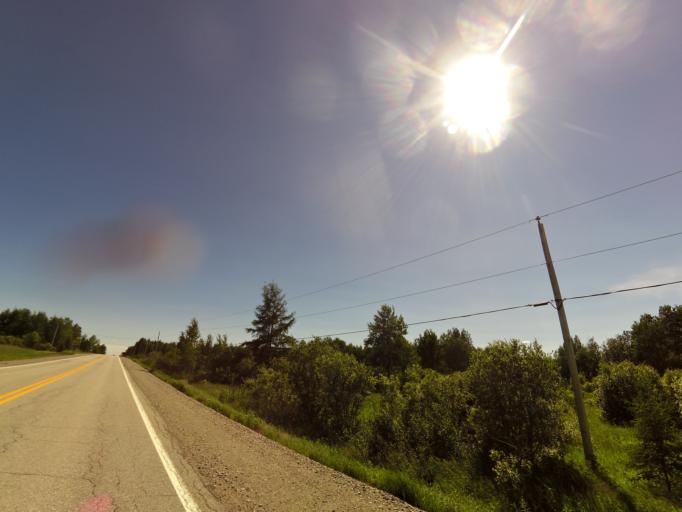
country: CA
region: Quebec
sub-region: Abitibi-Temiscamingue
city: Senneterre
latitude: 48.3042
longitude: -77.3058
